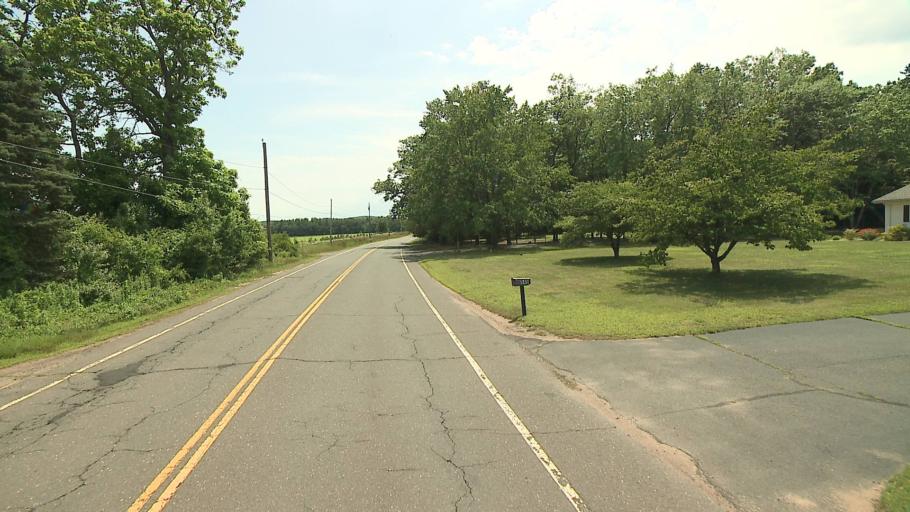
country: US
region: Massachusetts
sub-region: Hampden County
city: Southwick
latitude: 42.0338
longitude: -72.7502
